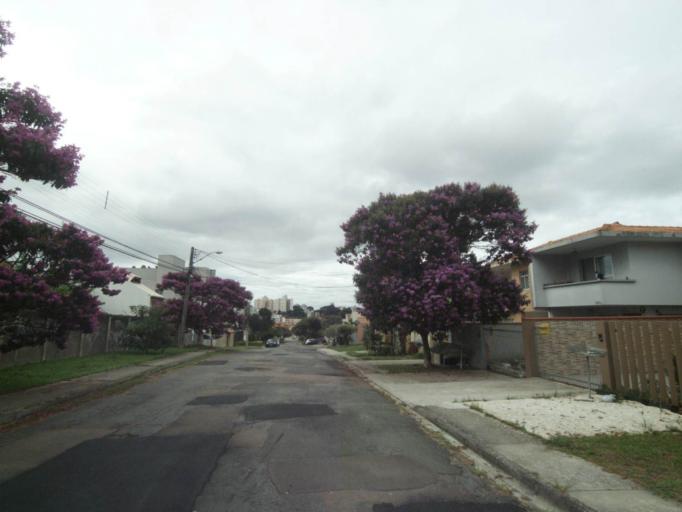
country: BR
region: Parana
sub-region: Curitiba
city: Curitiba
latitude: -25.4832
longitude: -49.2845
